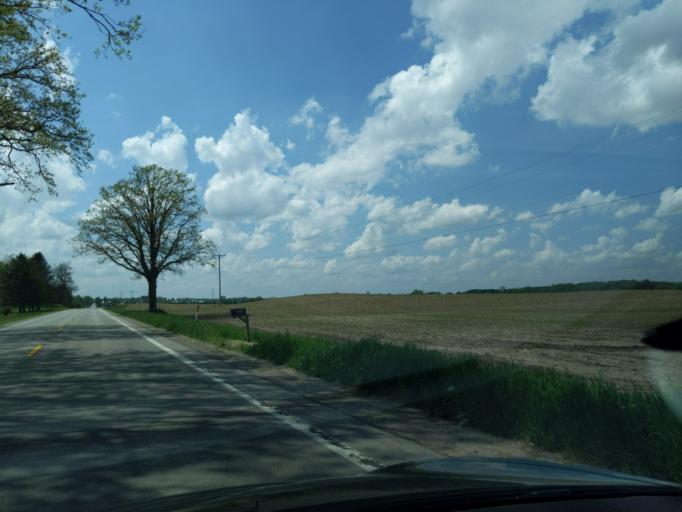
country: US
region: Michigan
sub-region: Ingham County
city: Williamston
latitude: 42.5558
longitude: -84.2732
